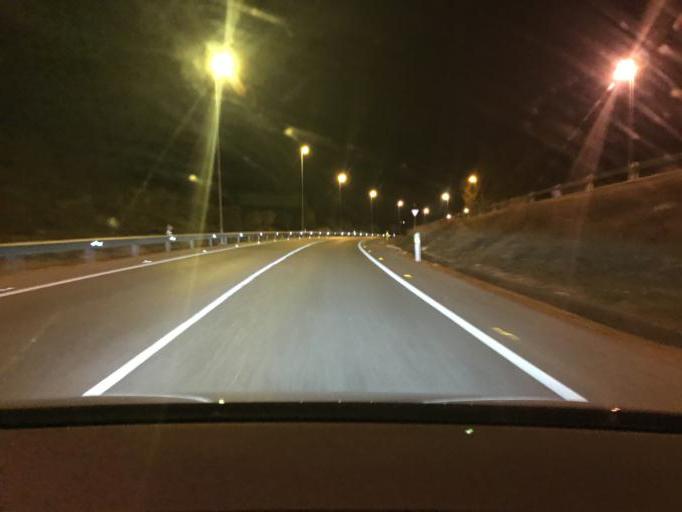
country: ES
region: Andalusia
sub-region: Provincia de Jaen
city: Jaen
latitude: 37.7815
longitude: -3.7548
